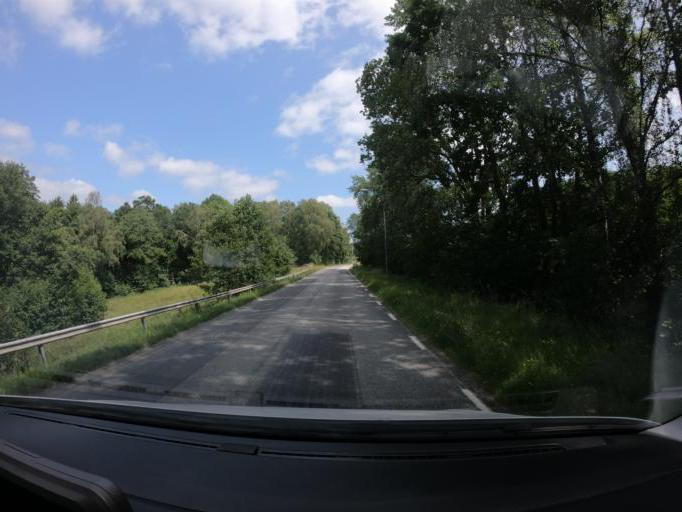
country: SE
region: Skane
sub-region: Hoors Kommun
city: Satofta
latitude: 55.9397
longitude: 13.5665
